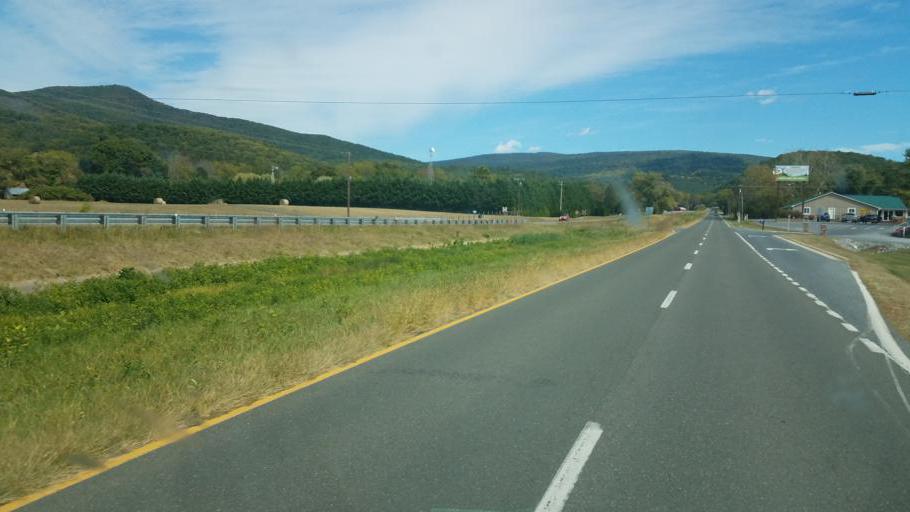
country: US
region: Virginia
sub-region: Page County
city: Luray
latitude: 38.6737
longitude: -78.3935
